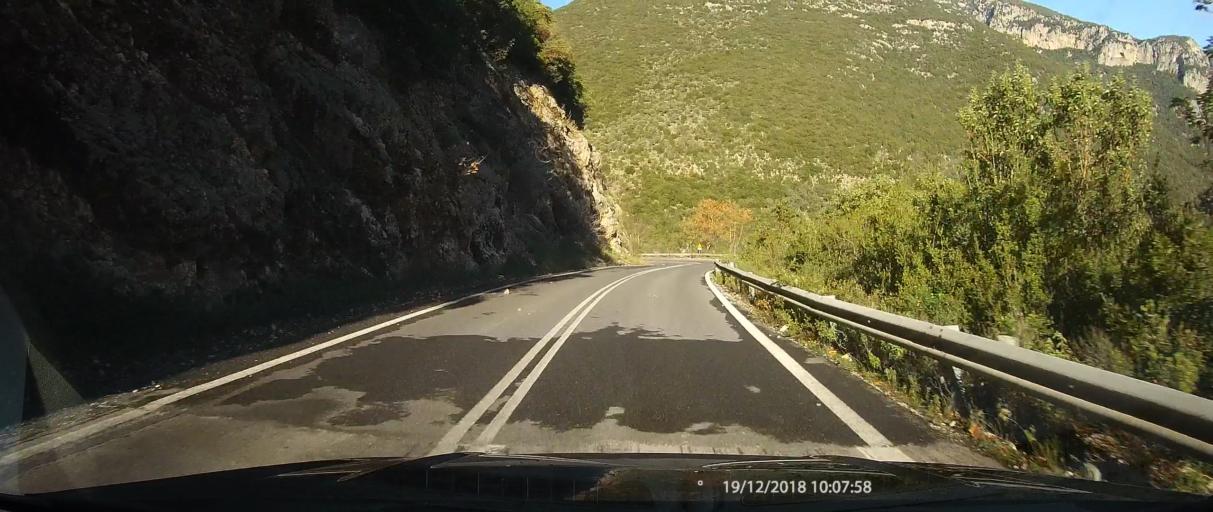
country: GR
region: Peloponnese
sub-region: Nomos Messinias
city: Paralia Vergas
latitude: 37.1158
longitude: 22.2081
